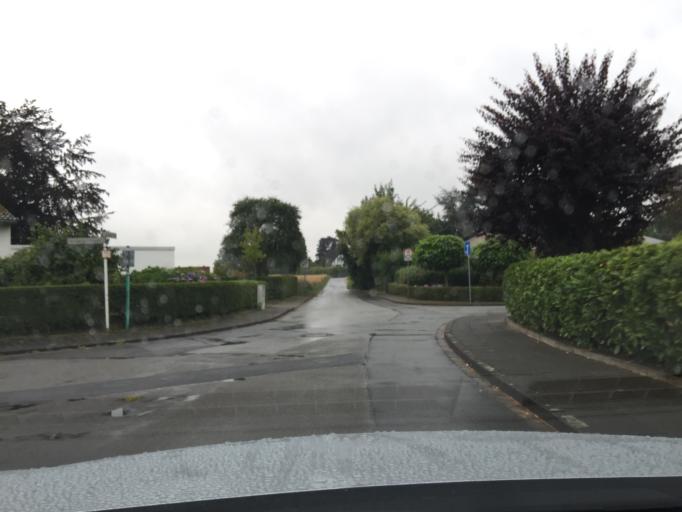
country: DE
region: North Rhine-Westphalia
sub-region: Regierungsbezirk Dusseldorf
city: Heiligenhaus
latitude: 51.3262
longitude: 6.9084
